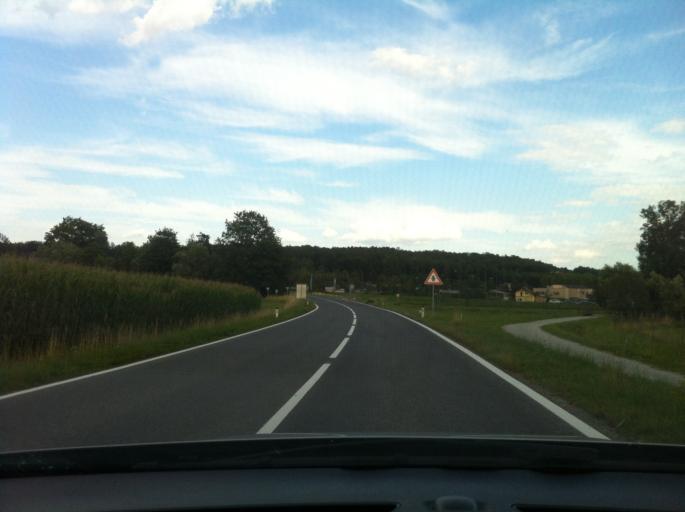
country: AT
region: Styria
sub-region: Politischer Bezirk Hartberg-Fuerstenfeld
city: Stubenberg
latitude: 47.2361
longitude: 15.7996
